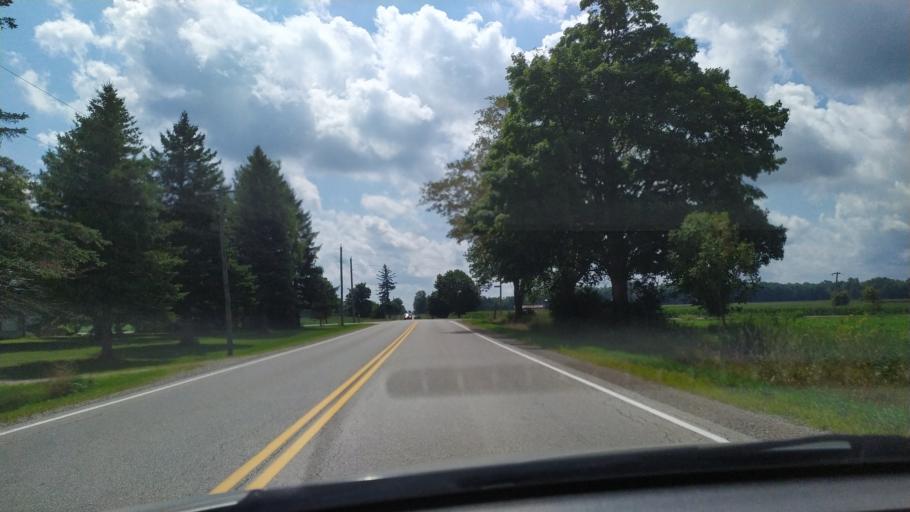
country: CA
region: Ontario
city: London
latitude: 43.0548
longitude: -81.3296
